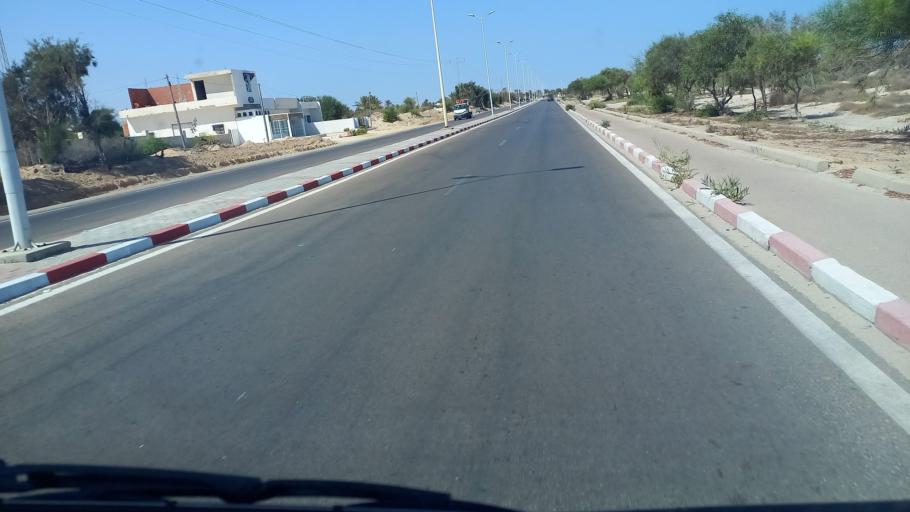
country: TN
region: Madanin
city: Midoun
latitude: 33.8692
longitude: 10.9512
